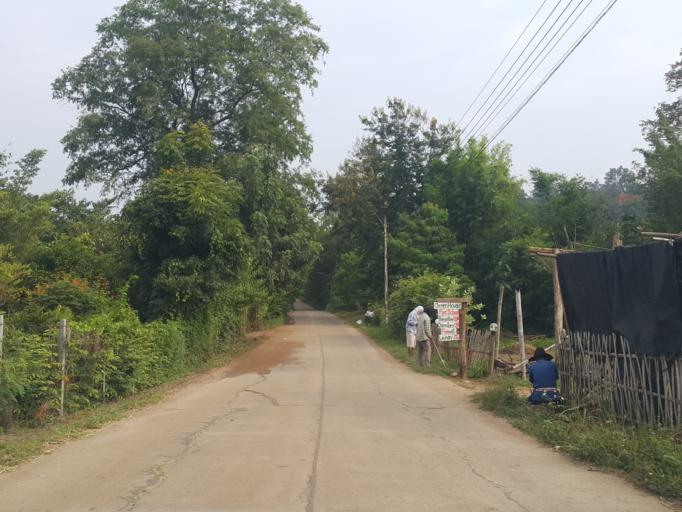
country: TH
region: Chiang Mai
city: Pai
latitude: 19.3661
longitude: 98.4498
